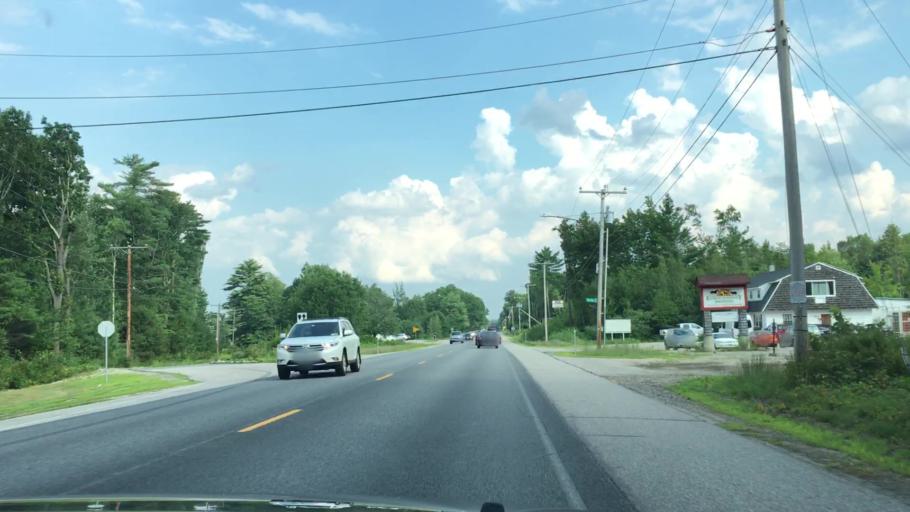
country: US
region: New Hampshire
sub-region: Strafford County
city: Farmington
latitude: 43.3999
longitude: -71.1074
